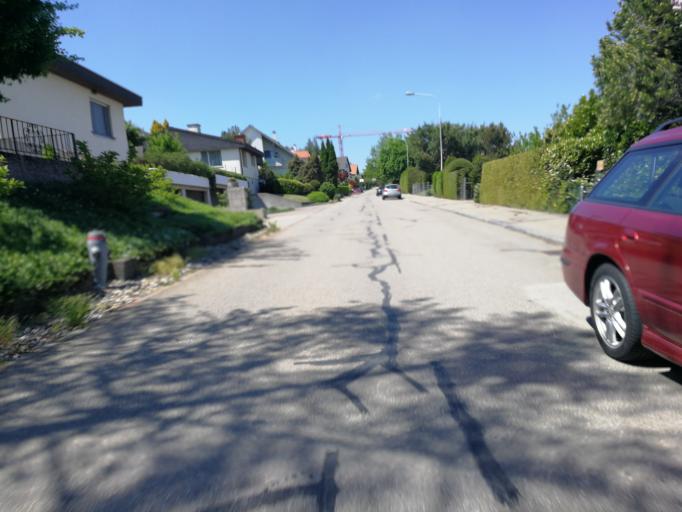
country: CH
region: Zurich
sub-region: Bezirk Uster
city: Aesch
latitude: 47.3215
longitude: 8.6581
